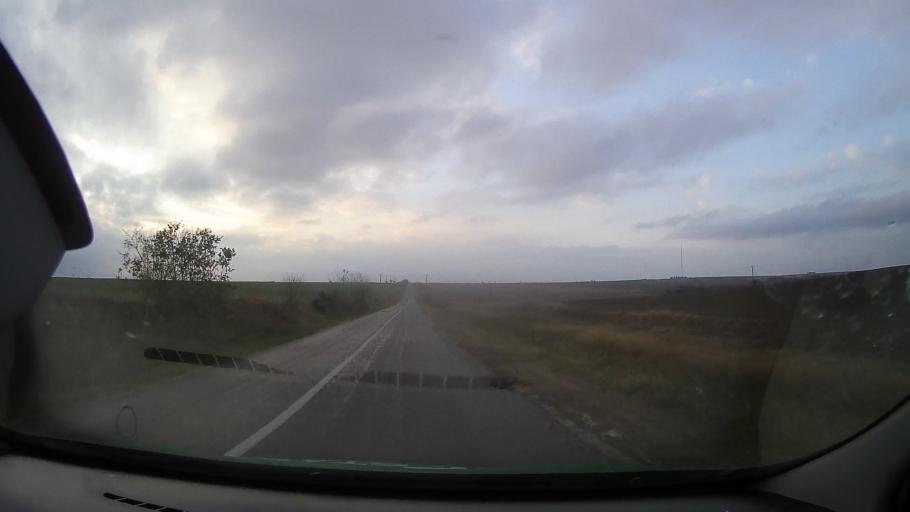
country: RO
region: Constanta
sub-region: Comuna Dobromir
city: Dobromir
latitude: 44.0326
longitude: 27.7696
